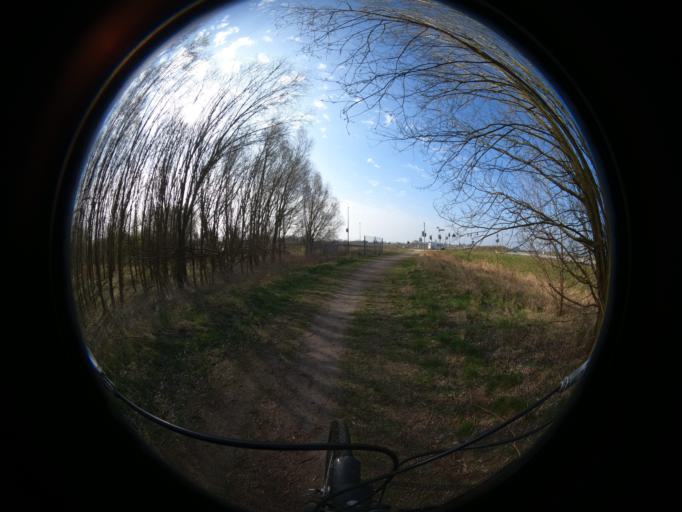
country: DE
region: Lower Saxony
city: Neu Wulmstorf
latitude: 53.5266
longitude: 9.8233
